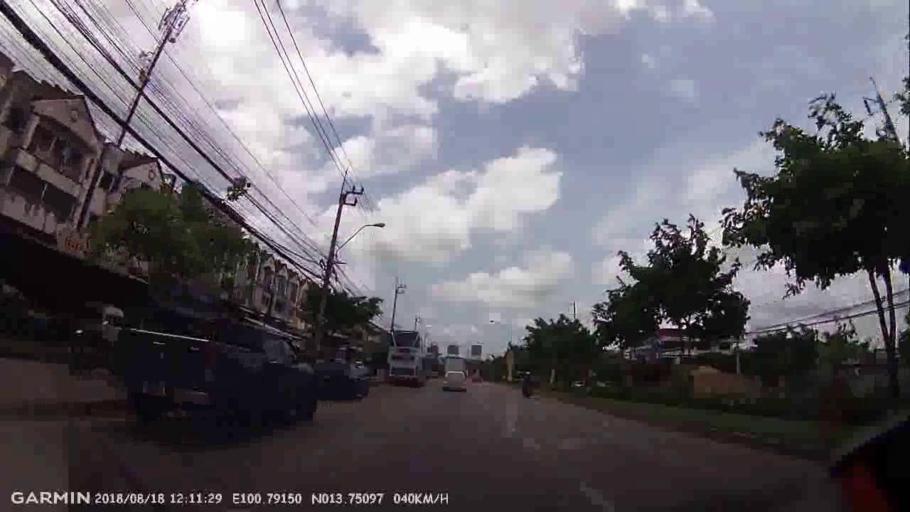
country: TH
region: Bangkok
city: Lat Krabang
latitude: 13.7511
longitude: 100.7913
